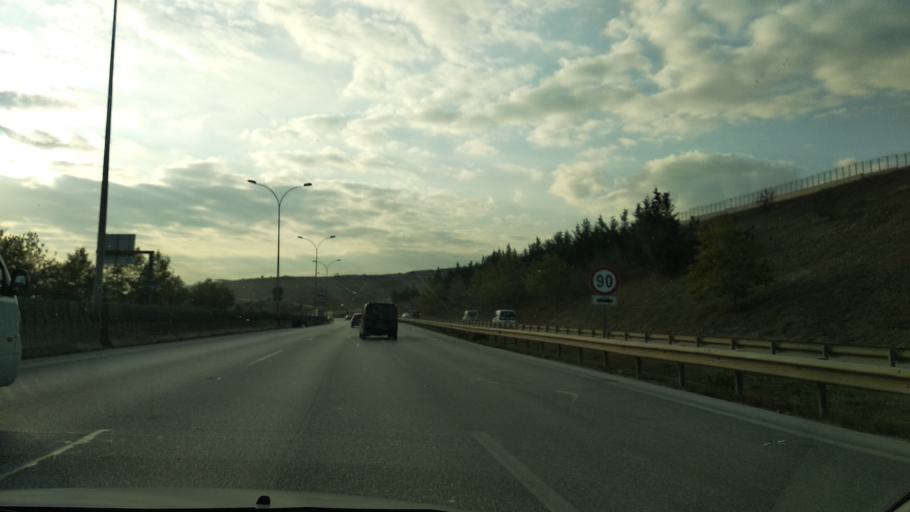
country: TR
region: Istanbul
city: Icmeler
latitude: 40.8777
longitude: 29.3087
